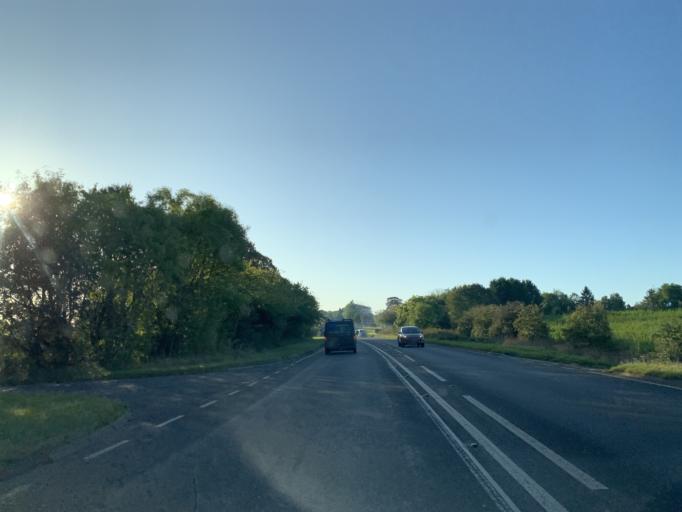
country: GB
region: England
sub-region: Wiltshire
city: Whiteparish
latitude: 50.9827
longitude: -1.6388
